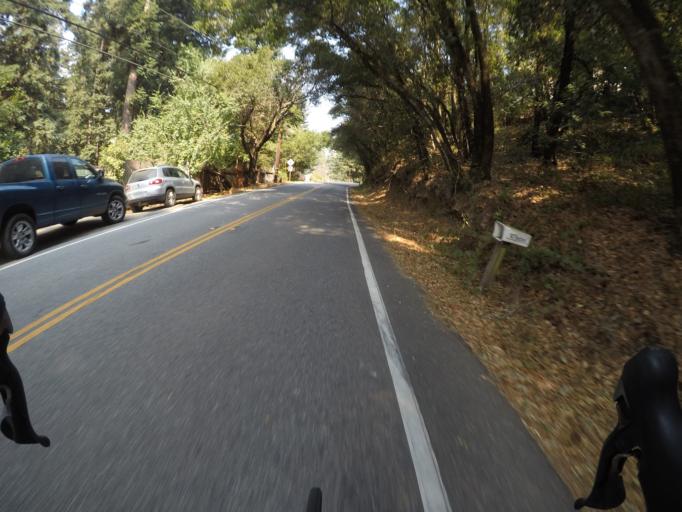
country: US
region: California
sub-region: Santa Cruz County
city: Scotts Valley
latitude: 37.0293
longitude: -122.0190
